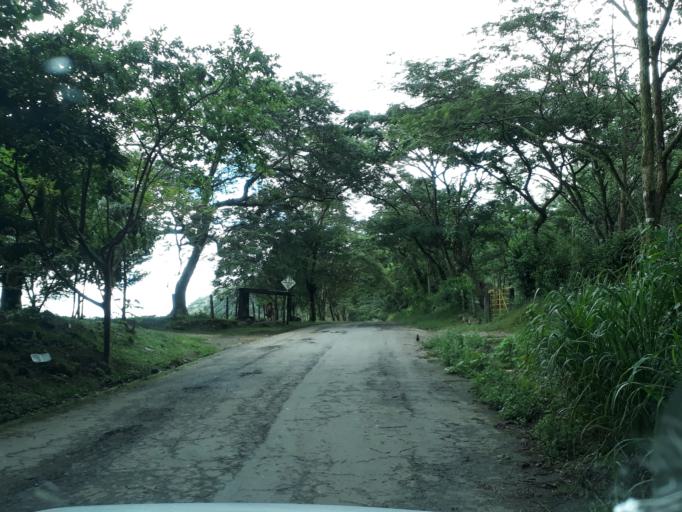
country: CO
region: Cundinamarca
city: Medina
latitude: 4.5623
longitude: -73.3635
